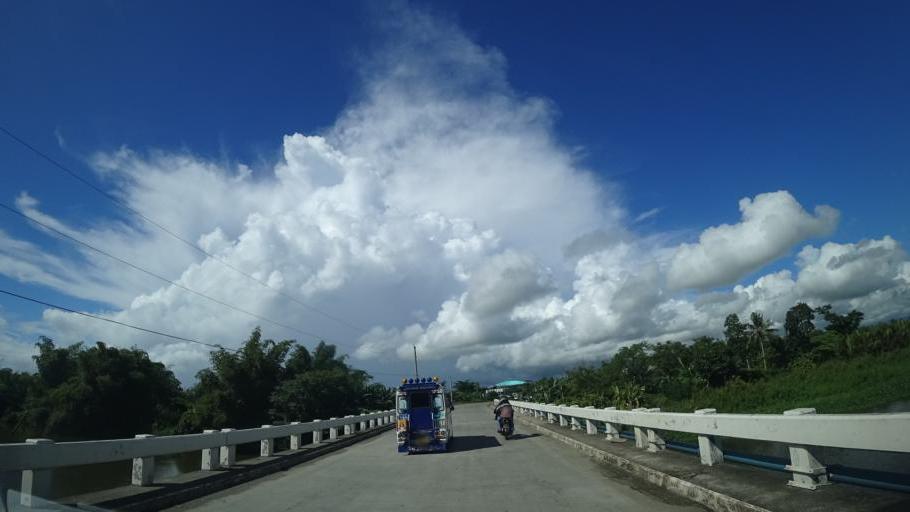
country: PH
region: Eastern Visayas
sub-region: Province of Leyte
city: Palo
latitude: 11.1601
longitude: 125.0032
